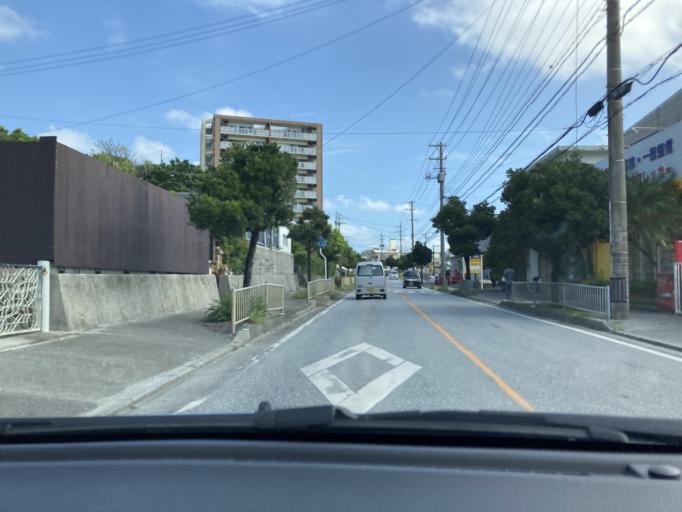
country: JP
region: Okinawa
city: Chatan
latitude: 26.2846
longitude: 127.7852
